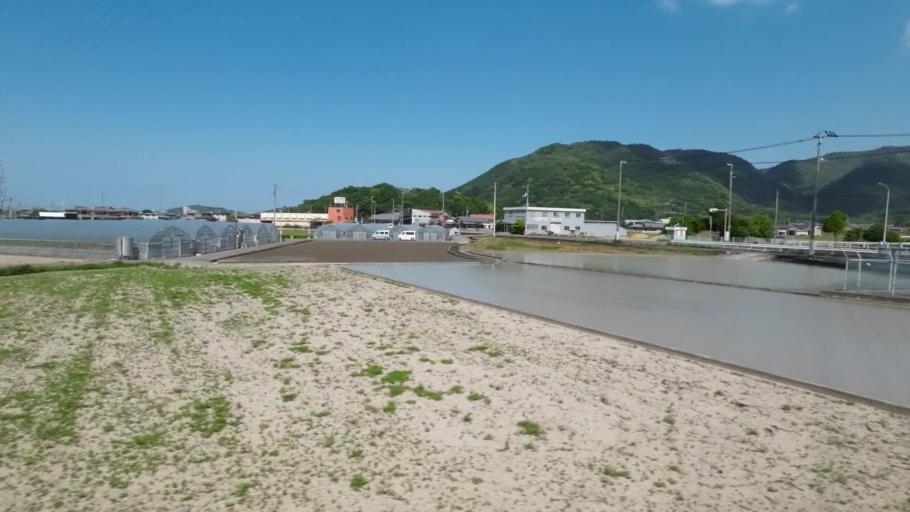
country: JP
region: Kagawa
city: Kan'onjicho
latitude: 34.1350
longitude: 133.6840
